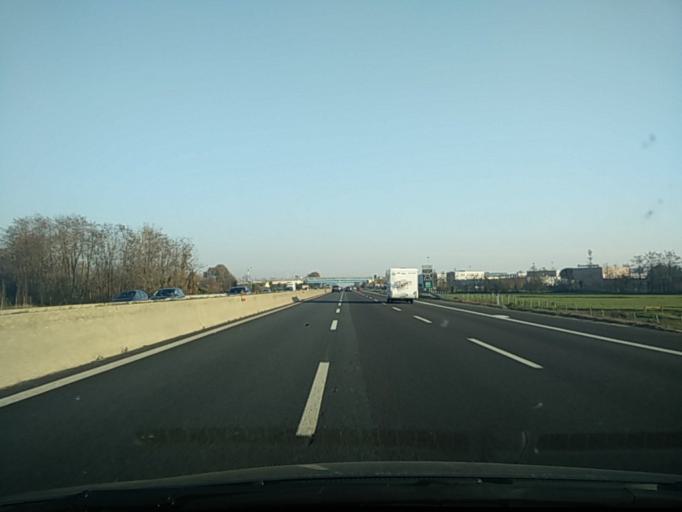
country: IT
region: Lombardy
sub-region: Provincia di Bergamo
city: Orio al Serio
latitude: 45.6674
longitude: 9.6837
